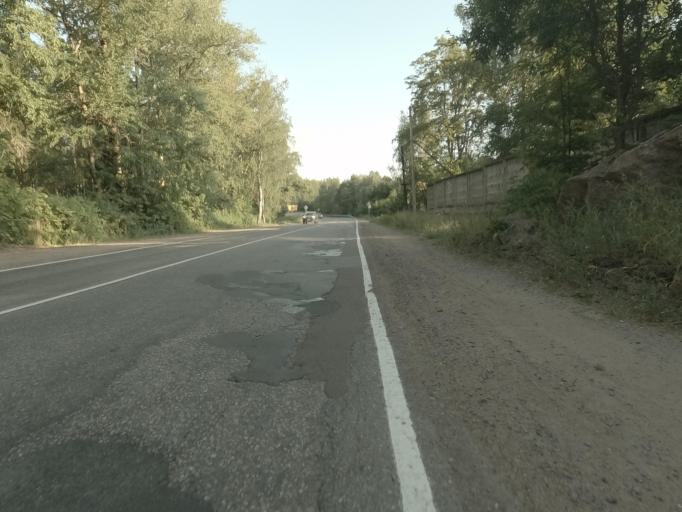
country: RU
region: Leningrad
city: Vyborg
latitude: 60.7312
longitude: 28.7593
